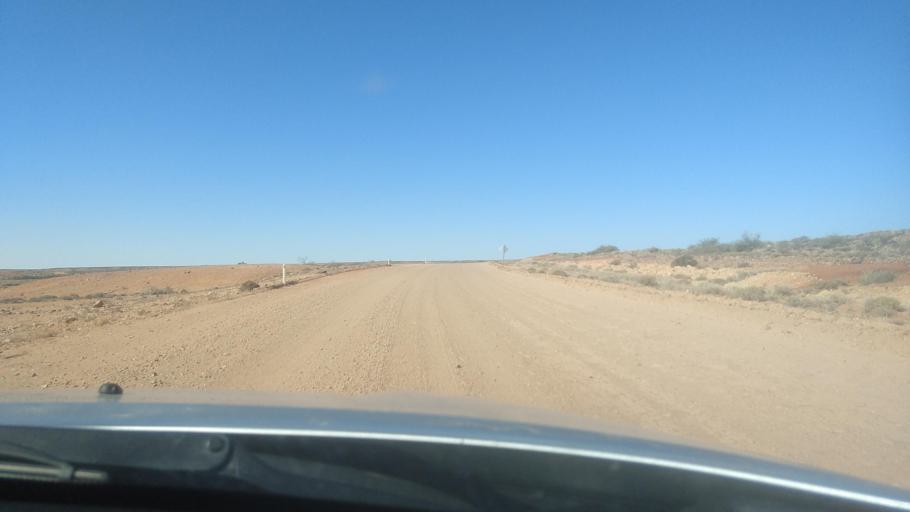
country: AU
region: South Australia
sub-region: Coober Pedy
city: Coober Pedy
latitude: -29.0321
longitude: 134.8164
